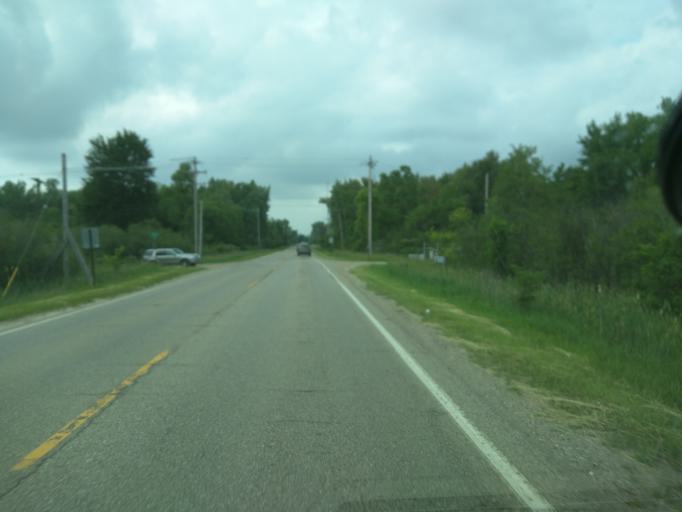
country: US
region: Michigan
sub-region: Ingham County
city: Edgemont Park
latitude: 42.7838
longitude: -84.6027
